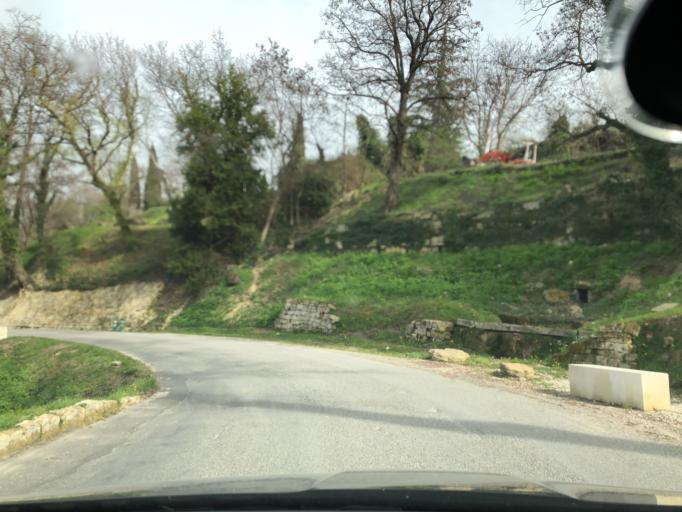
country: FR
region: Provence-Alpes-Cote d'Azur
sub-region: Departement du Vaucluse
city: Menerbes
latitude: 43.8311
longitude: 5.2087
